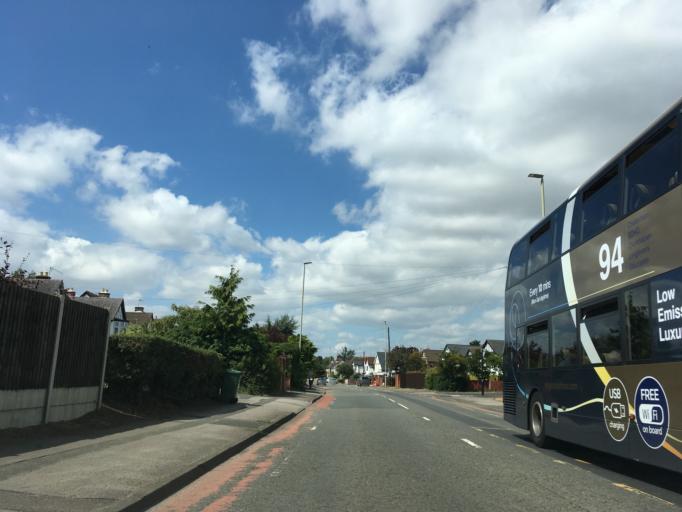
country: GB
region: England
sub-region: Gloucestershire
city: Barnwood
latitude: 51.8719
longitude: -2.2182
